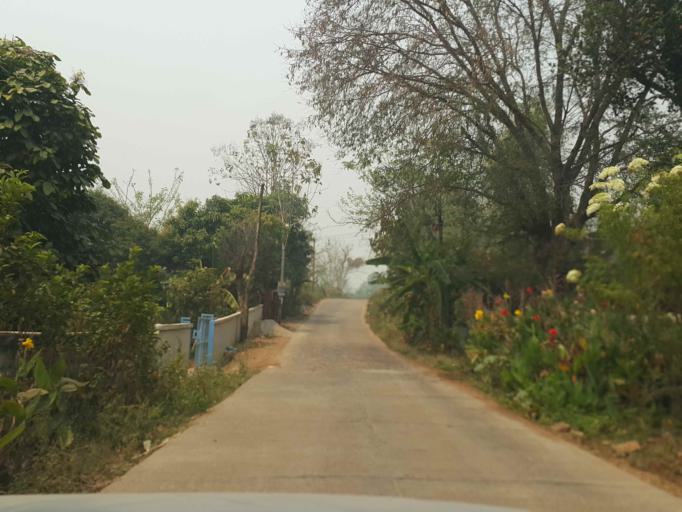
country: TH
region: Chiang Mai
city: Mae Taeng
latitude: 19.2187
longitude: 98.8563
